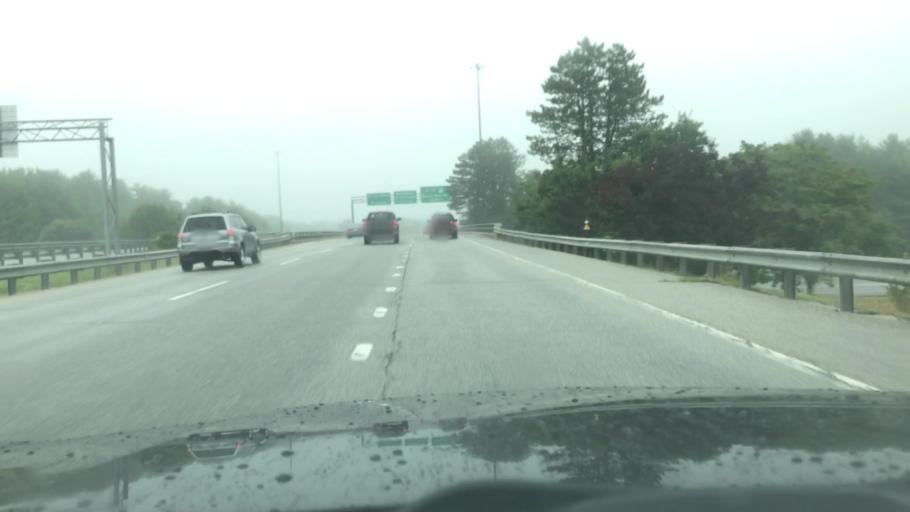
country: US
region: Maine
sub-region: Cumberland County
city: South Portland Gardens
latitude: 43.6229
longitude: -70.3199
